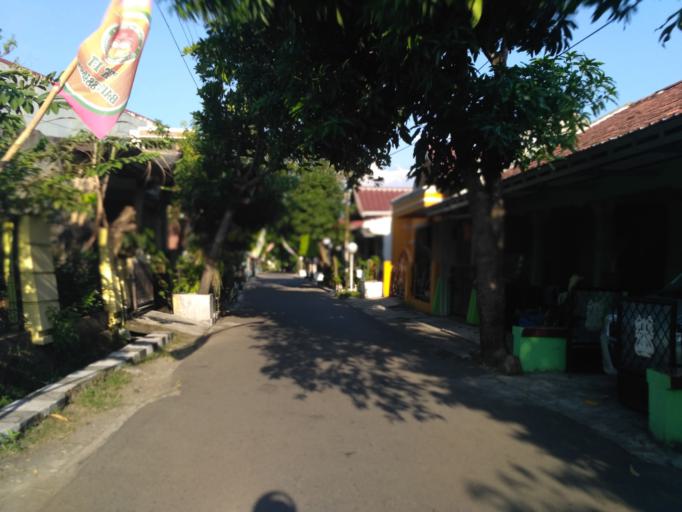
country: ID
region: Central Java
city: Mranggen
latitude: -7.0197
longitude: 110.4662
